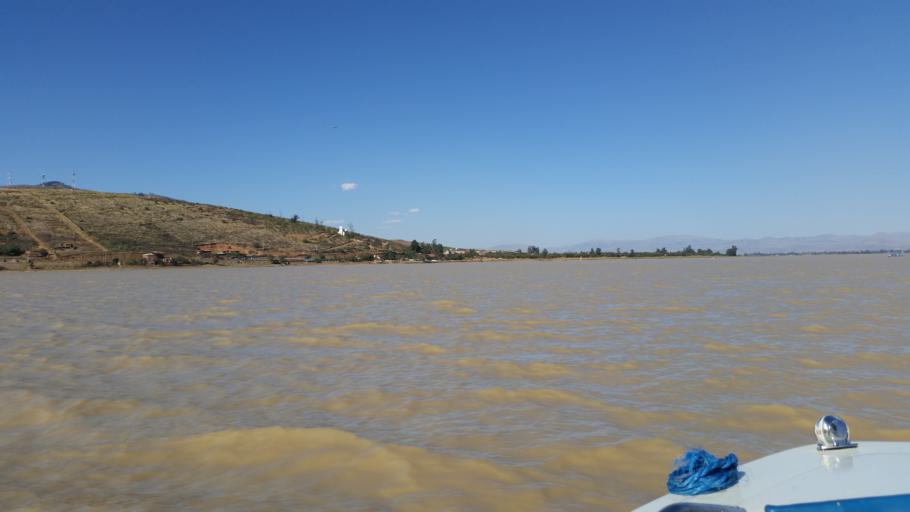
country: BO
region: Cochabamba
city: Tarata
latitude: -17.5354
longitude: -66.0915
